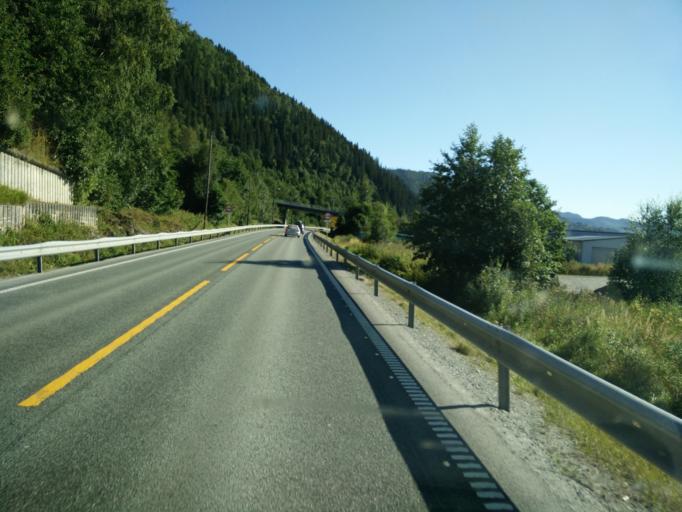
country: NO
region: Sor-Trondelag
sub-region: Orkdal
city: Orkanger
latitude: 63.2996
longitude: 9.8531
